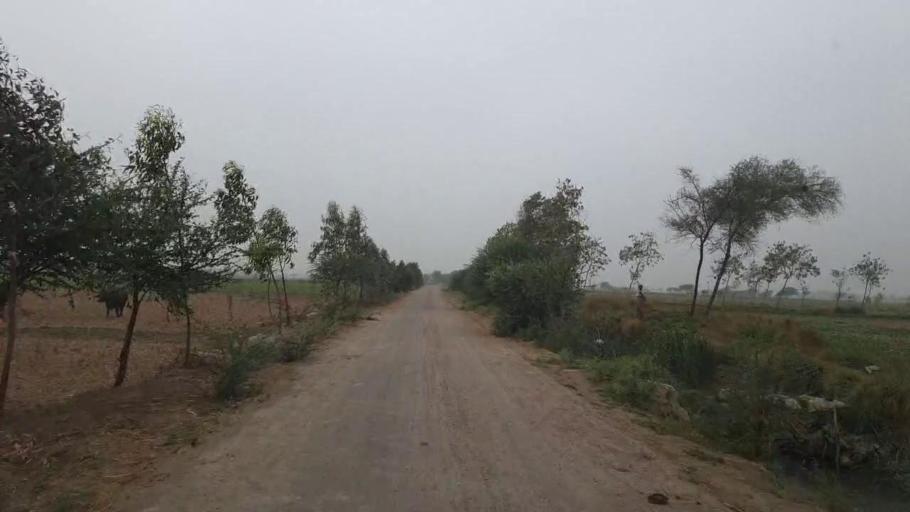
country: PK
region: Sindh
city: Badin
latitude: 24.5706
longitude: 68.6534
